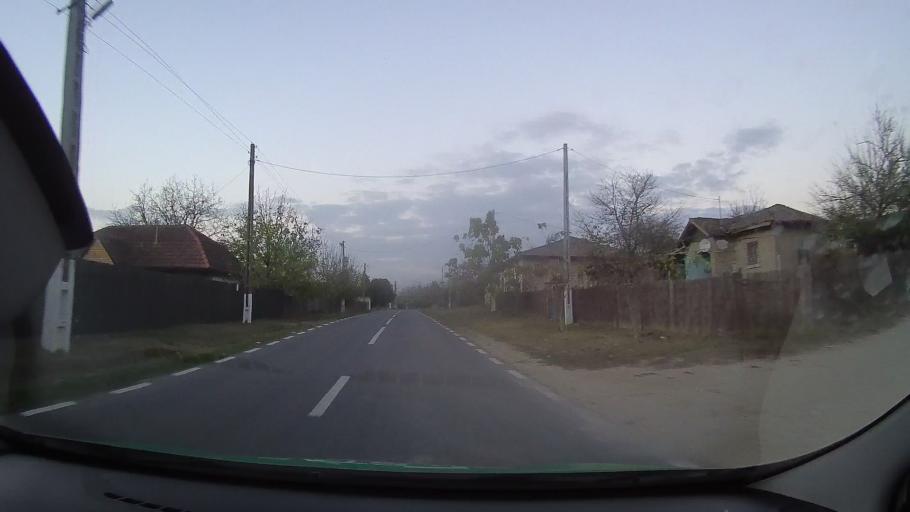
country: RO
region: Constanta
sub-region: Comuna Oltina
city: Oltina
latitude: 44.1685
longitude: 27.6662
